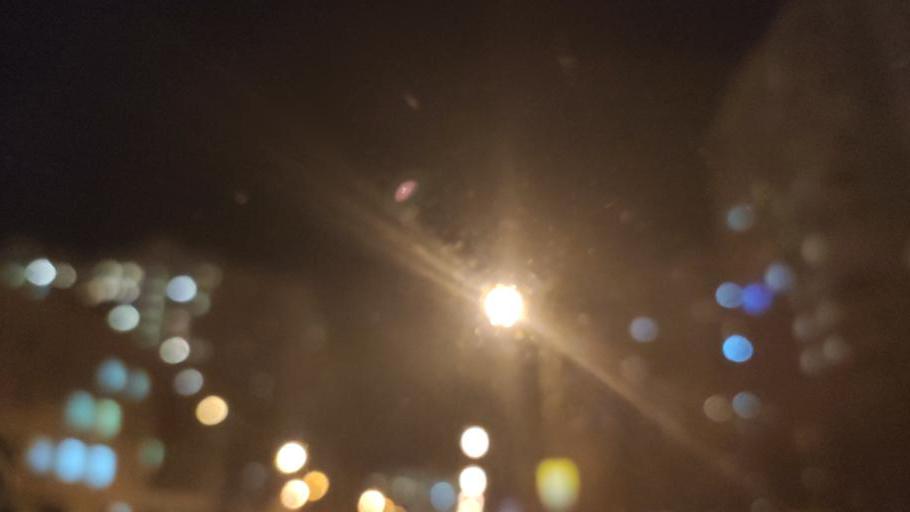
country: RU
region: Moskovskaya
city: Kommunarka
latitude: 55.5497
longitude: 37.5342
